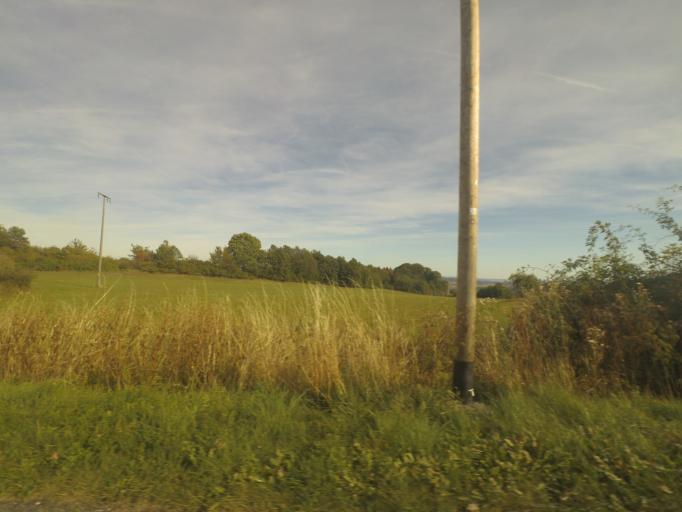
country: DE
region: Bavaria
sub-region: Regierungsbezirk Unterfranken
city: Hausen
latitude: 50.5004
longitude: 10.1141
